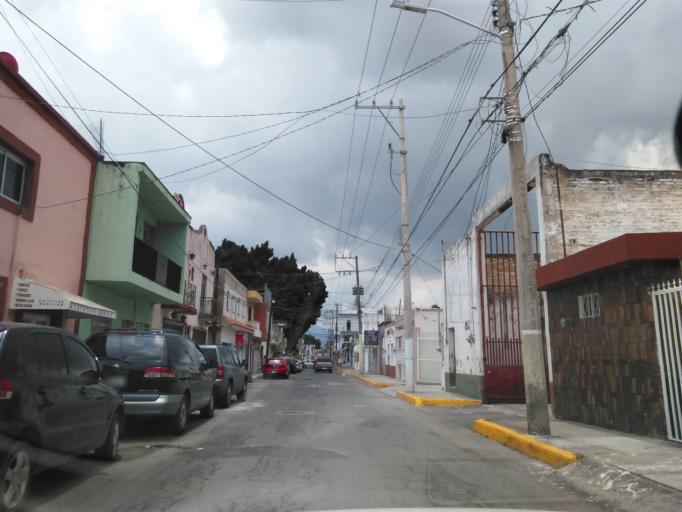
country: MX
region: Nayarit
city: Tepic
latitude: 21.5040
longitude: -104.8903
